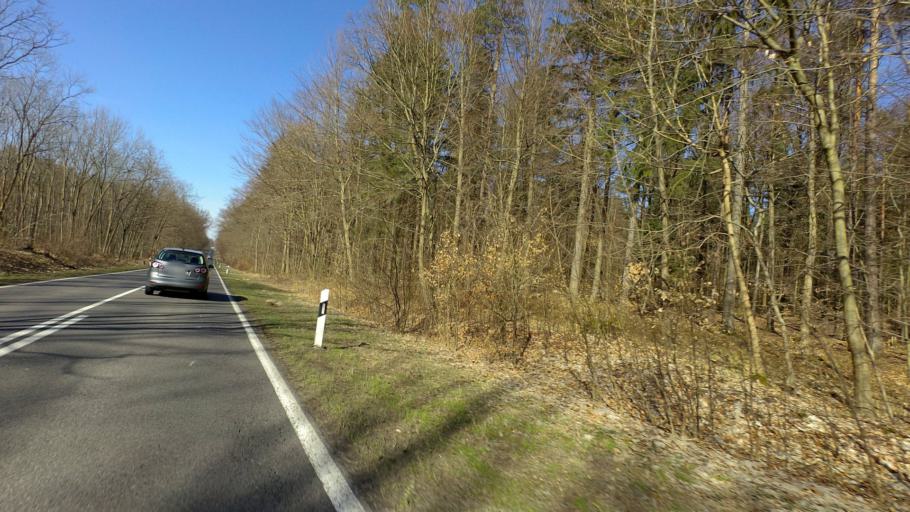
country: DE
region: Brandenburg
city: Eberswalde
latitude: 52.8088
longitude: 13.8345
